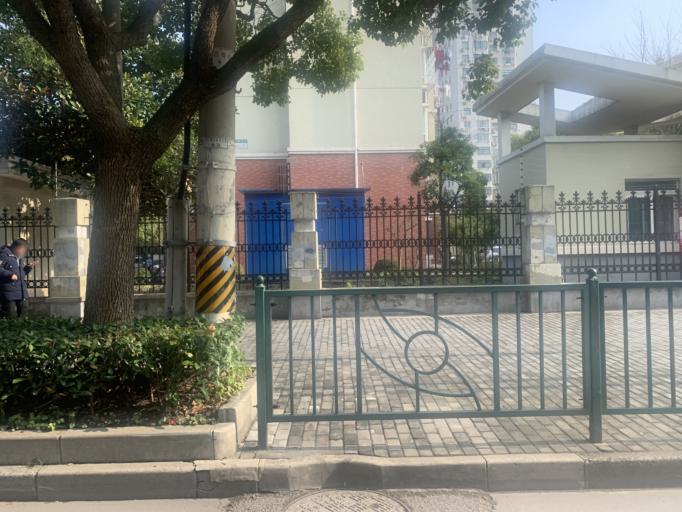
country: CN
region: Shanghai Shi
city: Huamu
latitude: 31.1857
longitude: 121.5146
